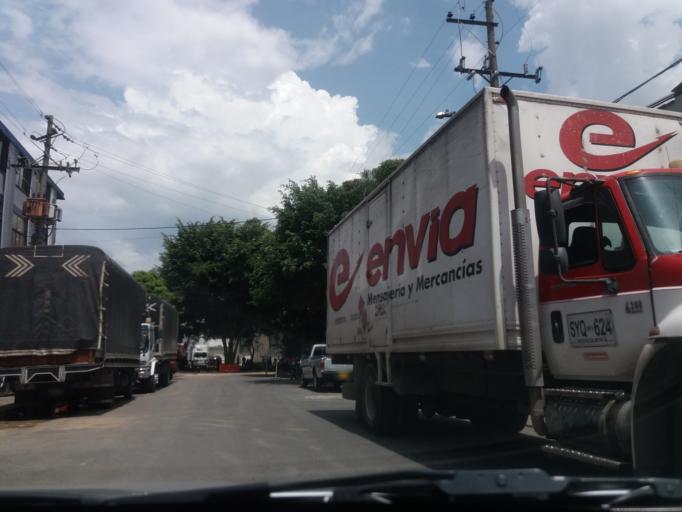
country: CO
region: Antioquia
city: Itagui
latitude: 6.1955
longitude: -75.5897
